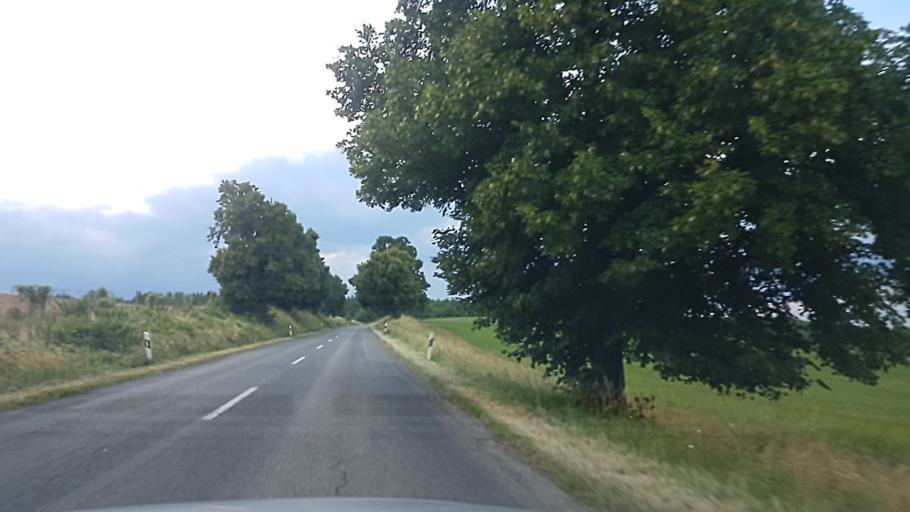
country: HU
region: Somogy
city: Kaposvar
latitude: 46.2568
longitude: 17.8329
